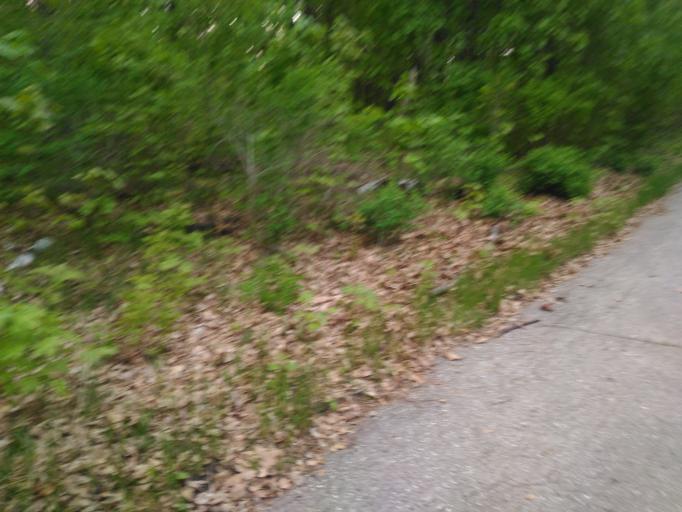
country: RU
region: Ulyanovsk
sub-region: Ulyanovskiy Rayon
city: Ulyanovsk
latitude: 54.2720
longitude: 48.3540
